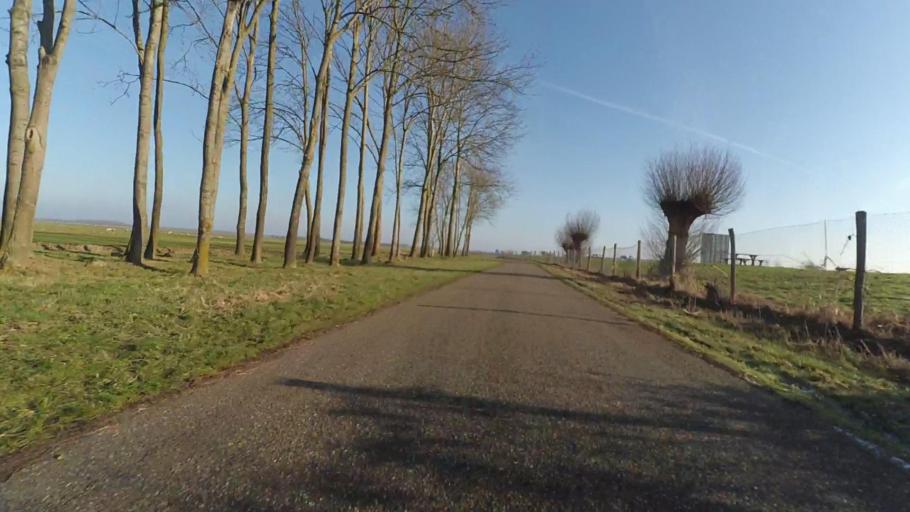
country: NL
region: Gelderland
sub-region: Gemeente Nijkerk
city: Nijkerk
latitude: 52.2488
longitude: 5.4922
